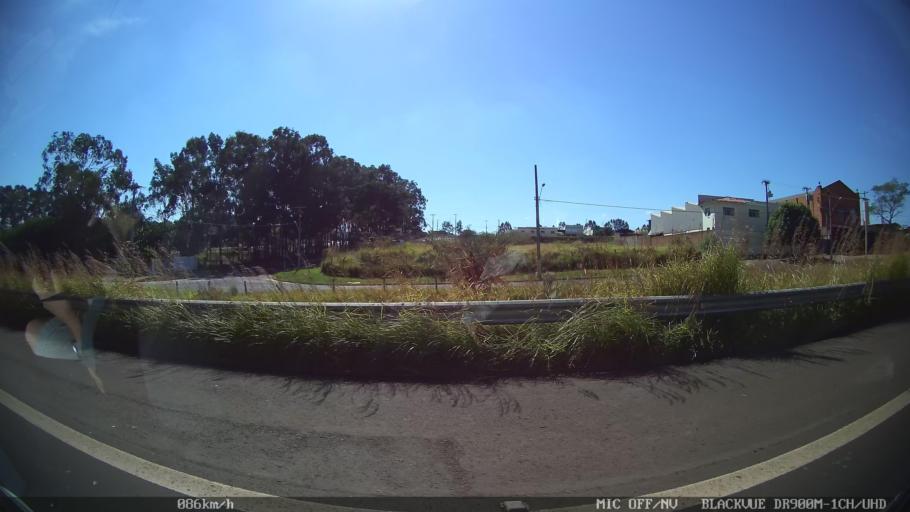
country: BR
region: Sao Paulo
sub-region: Franca
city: Franca
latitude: -20.5474
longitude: -47.4593
